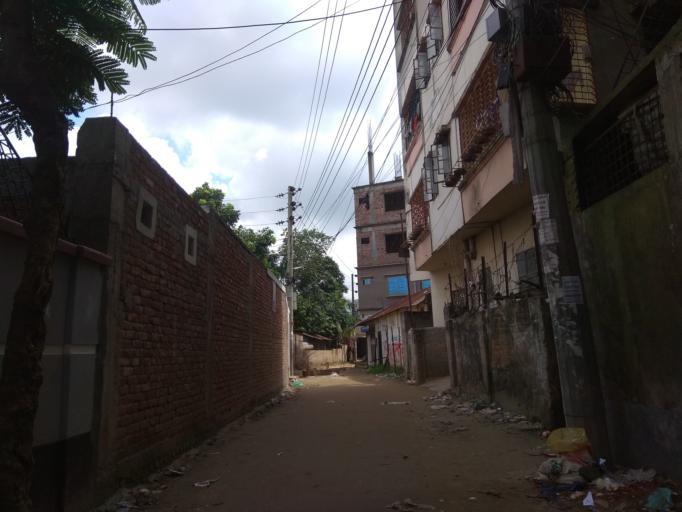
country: BD
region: Dhaka
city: Tungi
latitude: 23.8130
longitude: 90.3883
